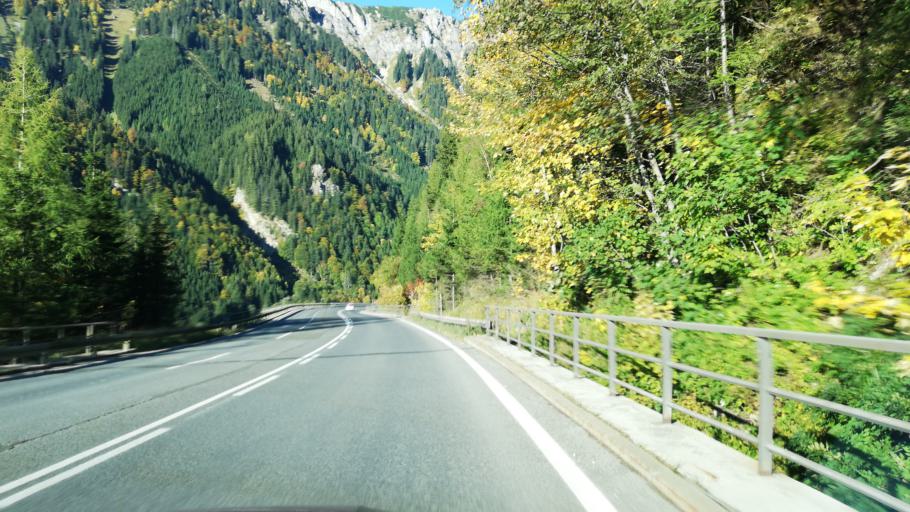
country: AT
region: Styria
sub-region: Politischer Bezirk Leoben
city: Eisenerz
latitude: 47.5442
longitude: 14.9307
